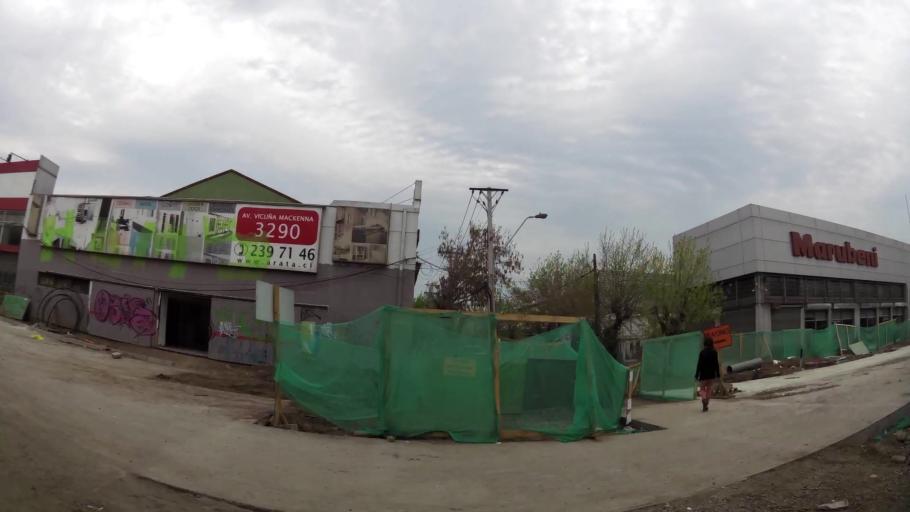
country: CL
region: Santiago Metropolitan
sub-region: Provincia de Santiago
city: Santiago
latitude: -33.4817
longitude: -70.6213
